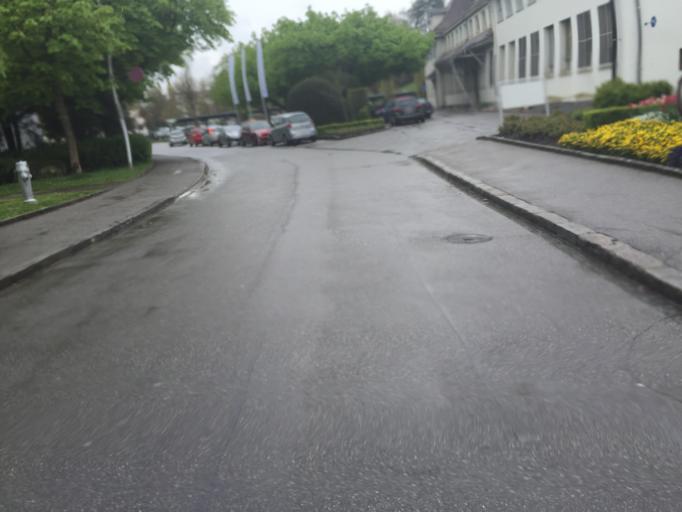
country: CH
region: Bern
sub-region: Bern-Mittelland District
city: Zollikofen
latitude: 46.9753
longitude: 7.4534
